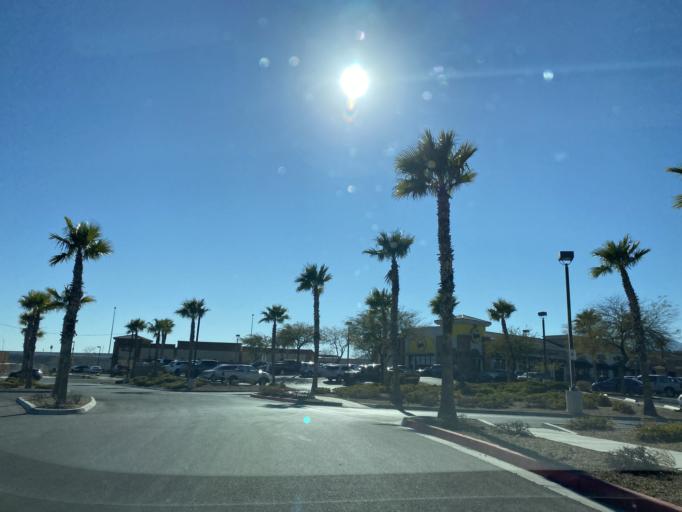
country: US
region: Nevada
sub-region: Clark County
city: Summerlin South
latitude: 36.2818
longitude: -115.2853
